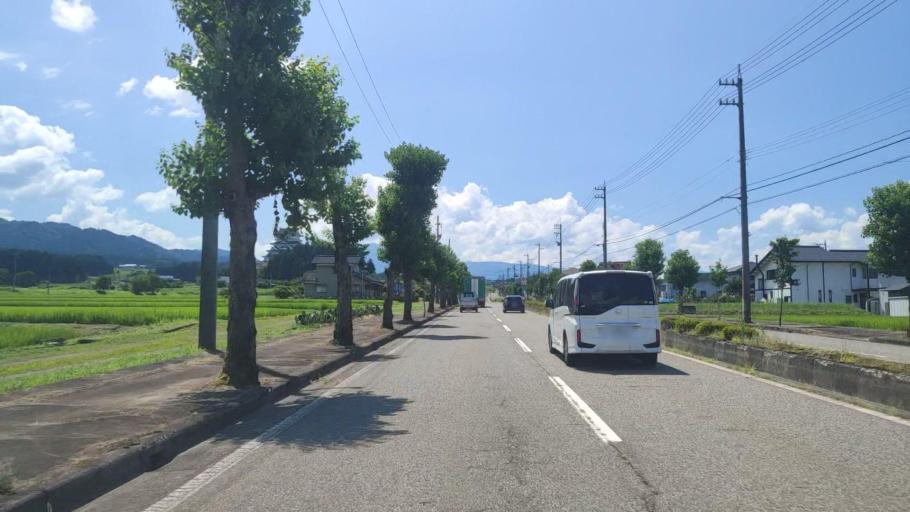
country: JP
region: Fukui
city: Katsuyama
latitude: 36.0475
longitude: 136.5158
